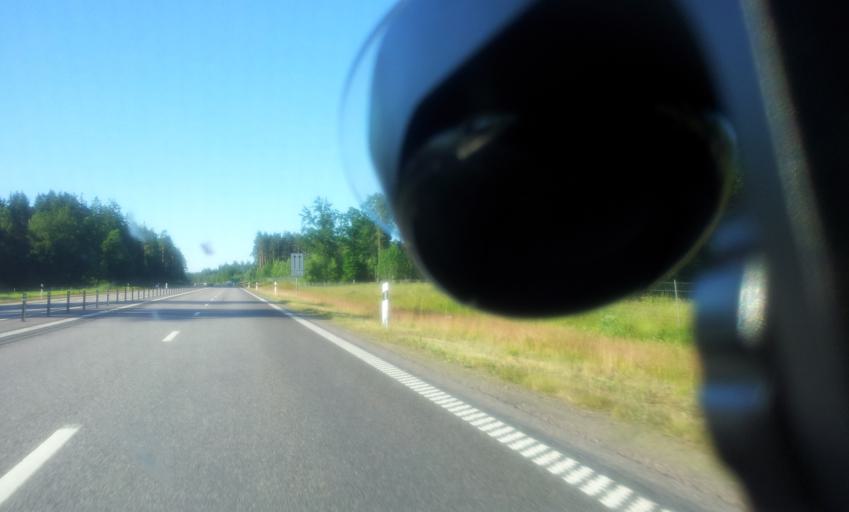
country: SE
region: Kalmar
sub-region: Kalmar Kommun
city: Ljungbyholm
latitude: 56.5507
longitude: 16.0854
